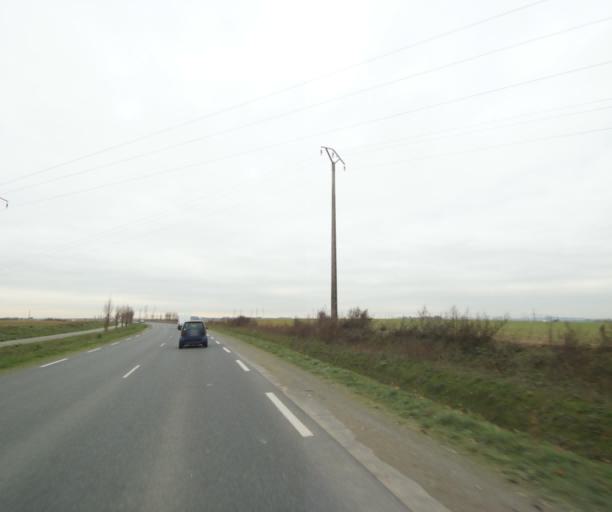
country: FR
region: Ile-de-France
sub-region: Departement du Val-d'Oise
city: Arnouville
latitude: 49.0073
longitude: 2.4258
